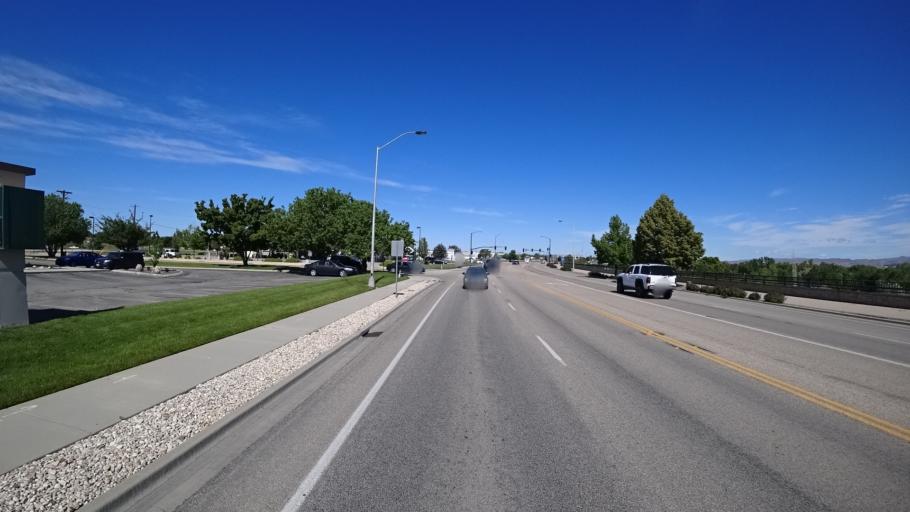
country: US
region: Idaho
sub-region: Ada County
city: Boise
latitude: 43.5726
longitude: -116.1906
